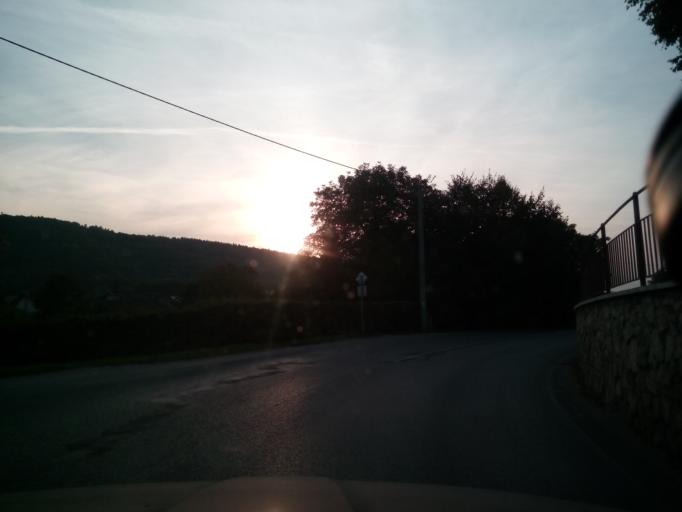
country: SK
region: Presovsky
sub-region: Okres Bardejov
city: Bardejov
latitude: 49.3013
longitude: 21.3168
